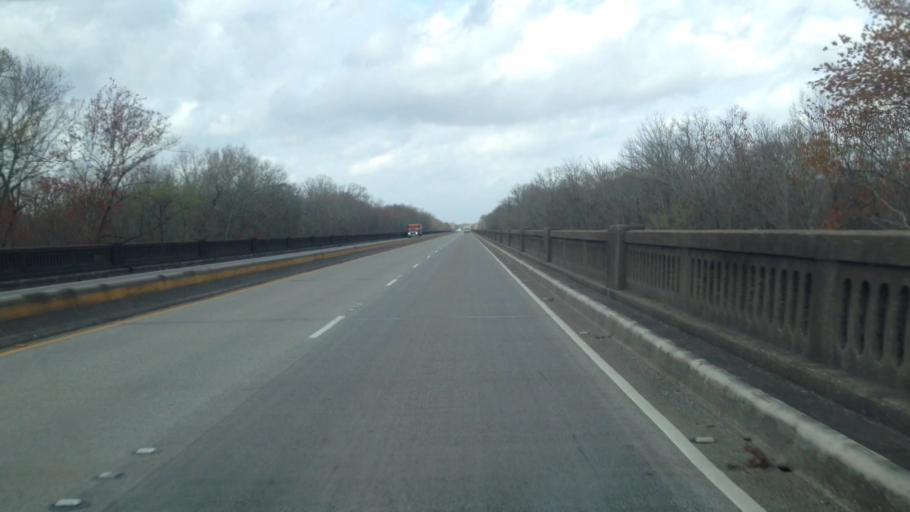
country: US
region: Louisiana
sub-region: Saint Landry Parish
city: Krotz Springs
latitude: 30.5534
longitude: -91.7065
